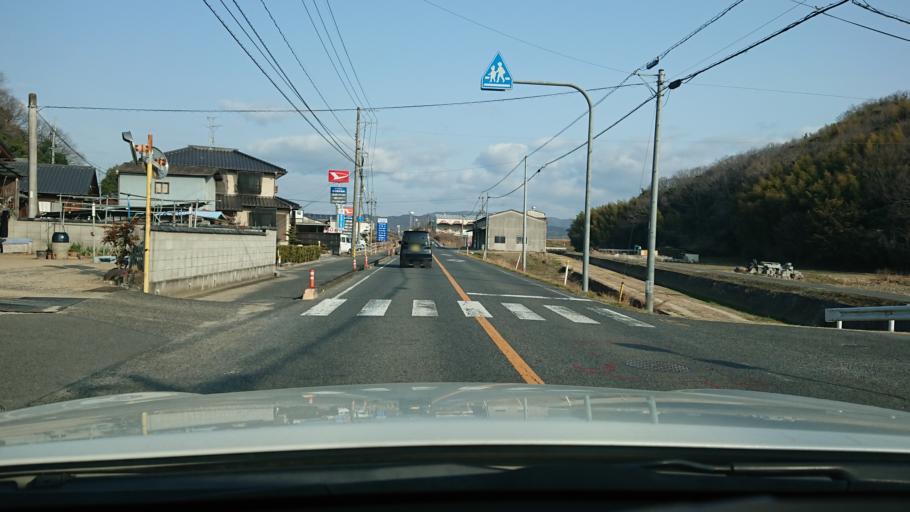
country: JP
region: Okayama
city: Soja
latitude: 34.6214
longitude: 133.7062
